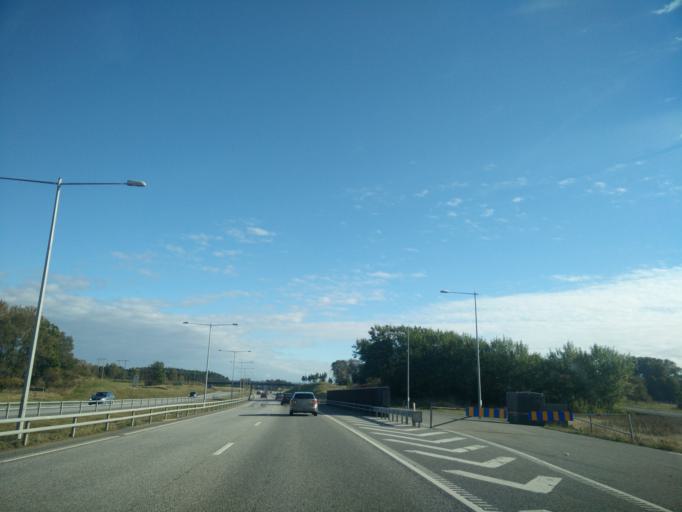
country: SE
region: Stockholm
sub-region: Taby Kommun
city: Taby
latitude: 59.4745
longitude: 18.0141
